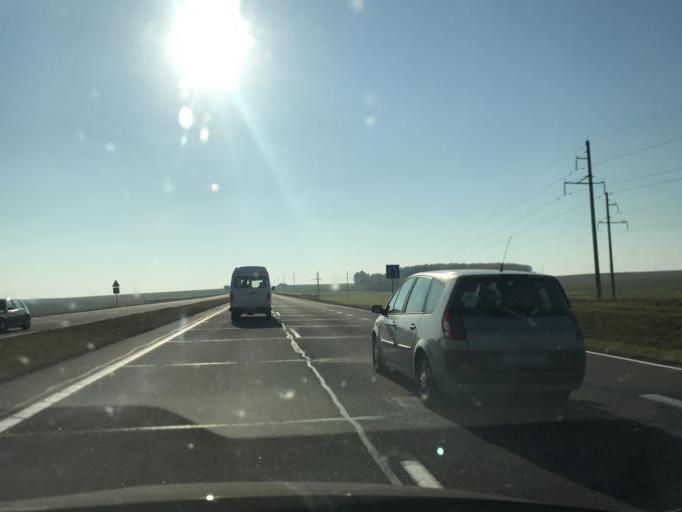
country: BY
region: Minsk
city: Novy Svyerzhan'
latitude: 53.4777
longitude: 26.6253
